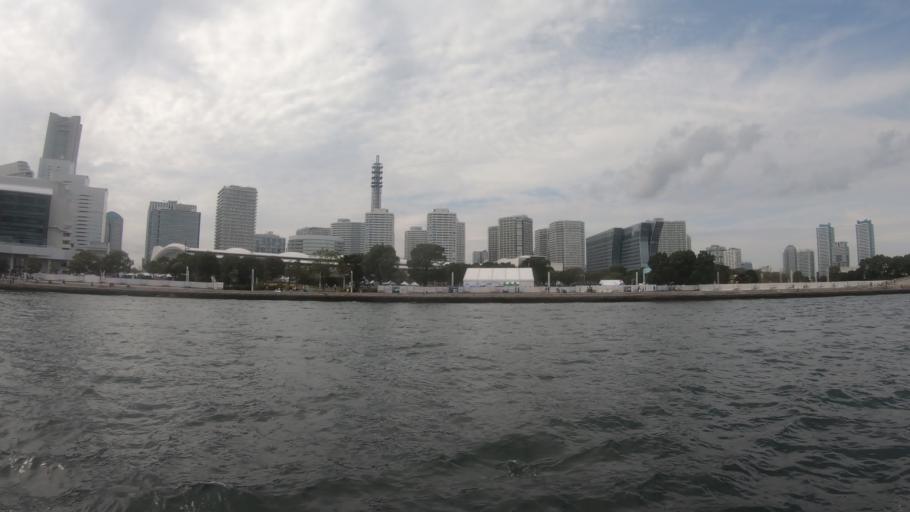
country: JP
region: Kanagawa
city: Yokohama
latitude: 35.4604
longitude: 139.6392
